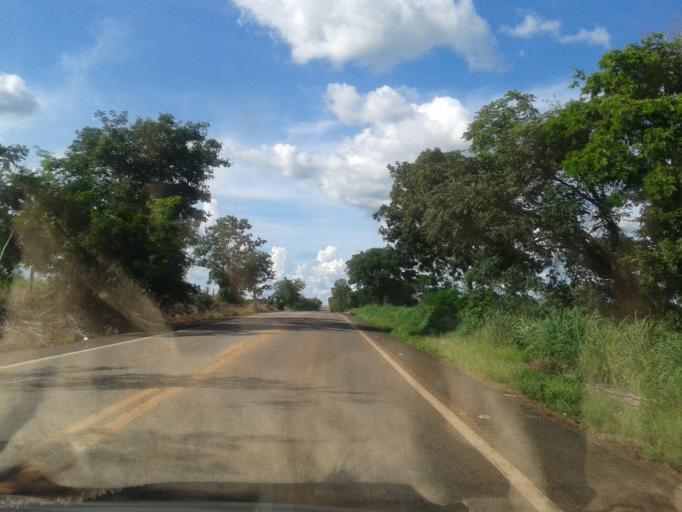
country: BR
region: Goias
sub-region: Mozarlandia
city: Mozarlandia
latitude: -14.7397
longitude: -50.5435
